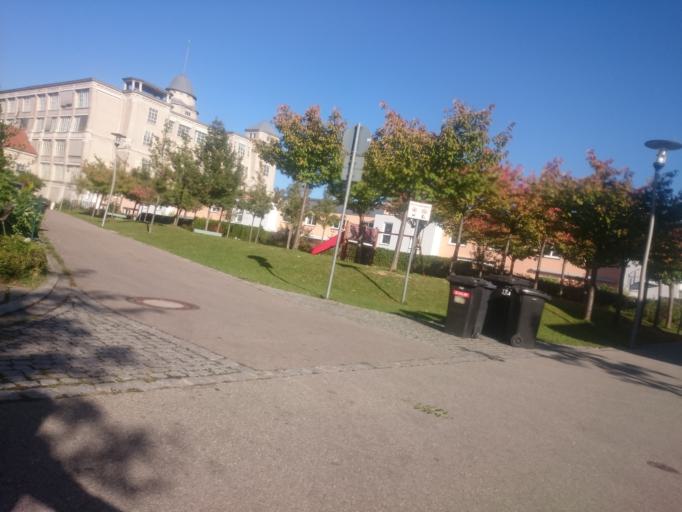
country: DE
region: Bavaria
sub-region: Swabia
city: Augsburg
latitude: 48.3664
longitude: 10.9212
